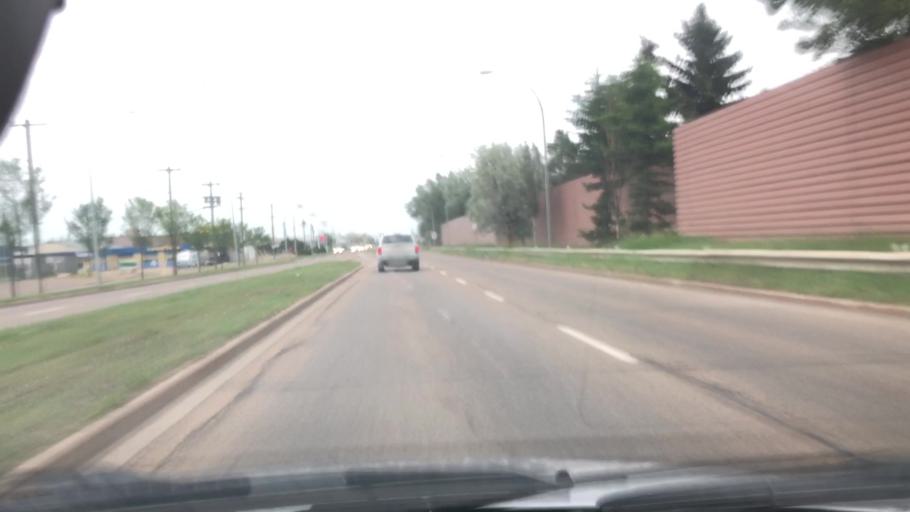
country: CA
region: Alberta
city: St. Albert
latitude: 53.5589
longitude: -113.5965
